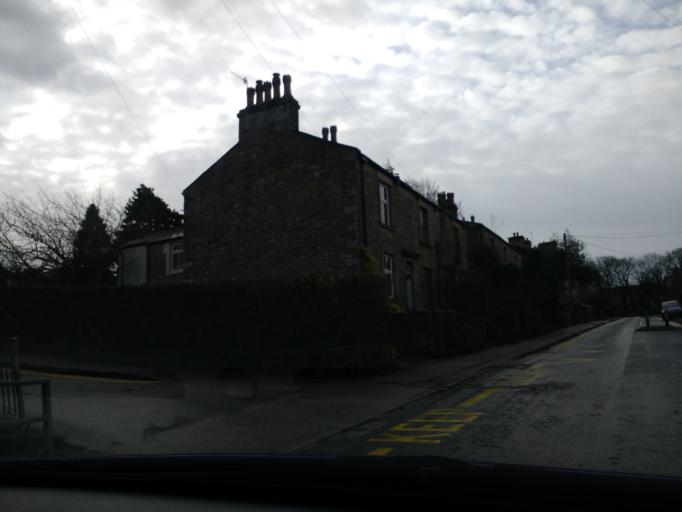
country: GB
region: England
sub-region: Lancashire
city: Lancaster
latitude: 54.0497
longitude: -2.7863
